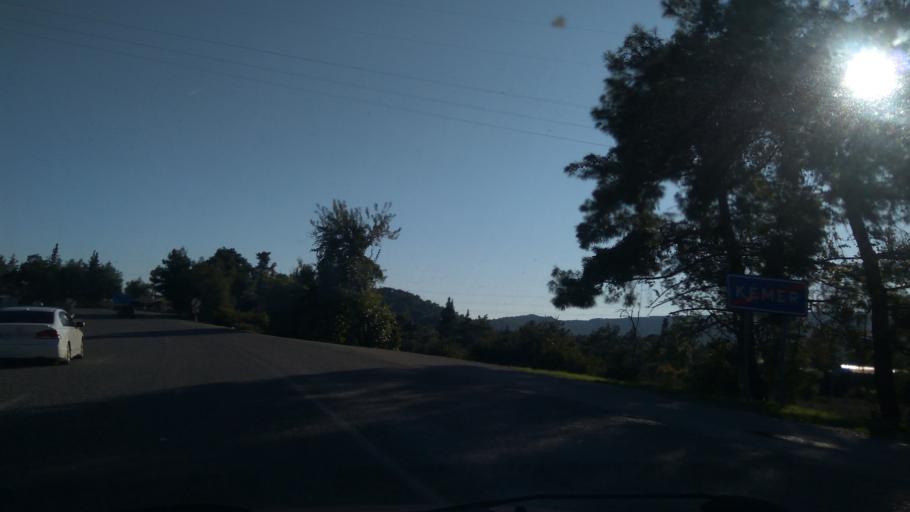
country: TR
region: Antalya
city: Kemer
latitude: 36.5854
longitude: 30.5425
